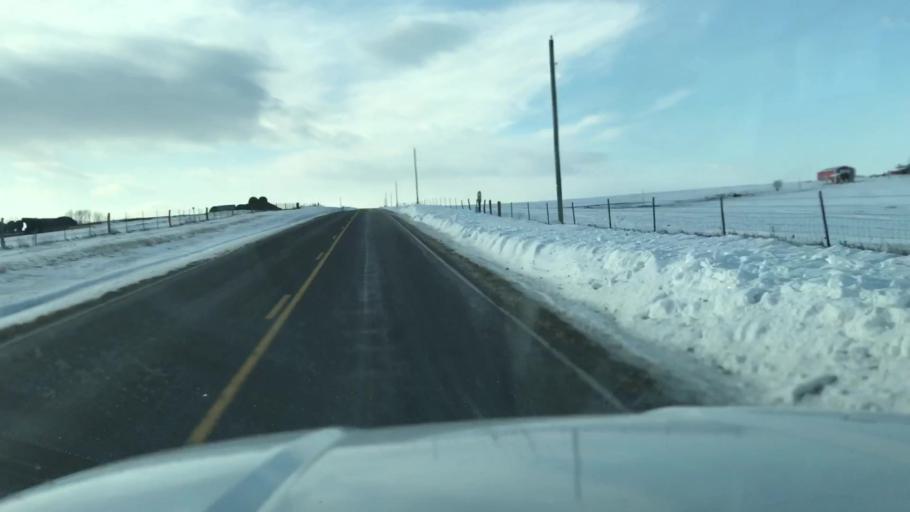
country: US
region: Missouri
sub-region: Nodaway County
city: Maryville
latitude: 40.2009
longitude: -94.9012
